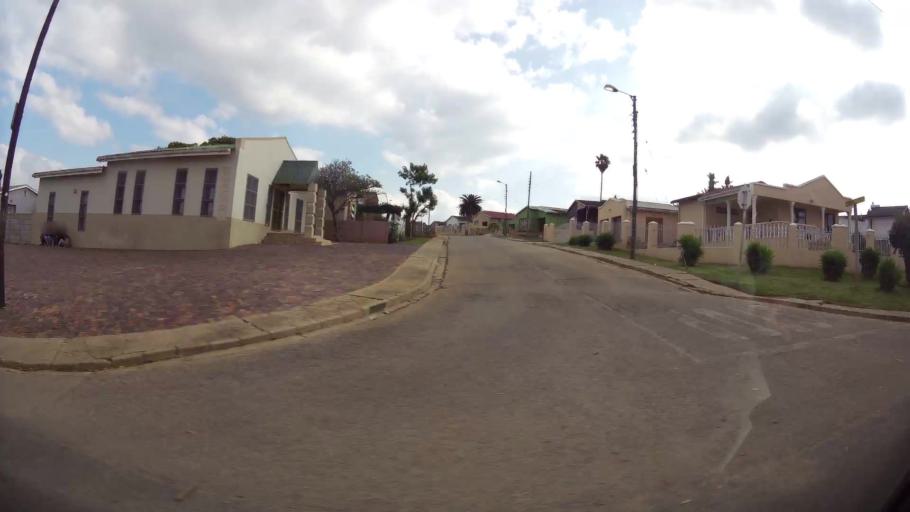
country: ZA
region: Eastern Cape
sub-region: Nelson Mandela Bay Metropolitan Municipality
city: Uitenhage
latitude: -33.7366
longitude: 25.3811
